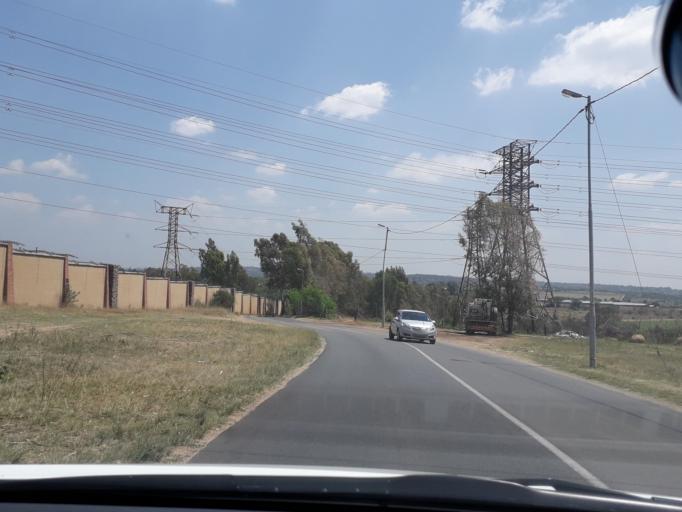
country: ZA
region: Gauteng
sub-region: City of Johannesburg Metropolitan Municipality
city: Midrand
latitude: -26.0161
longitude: 28.0736
